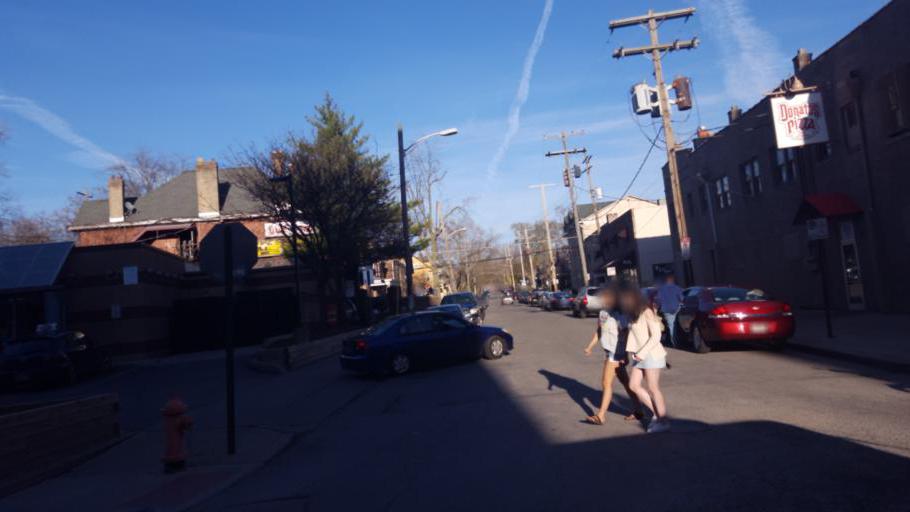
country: US
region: Ohio
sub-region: Franklin County
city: Grandview Heights
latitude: 40.0050
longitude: -83.0090
